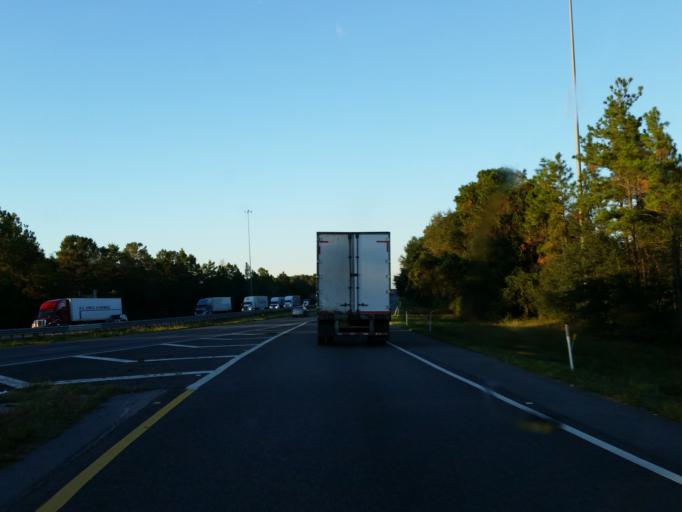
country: US
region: Florida
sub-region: Hernando County
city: Hill 'n Dale
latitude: 28.5256
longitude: -82.2368
